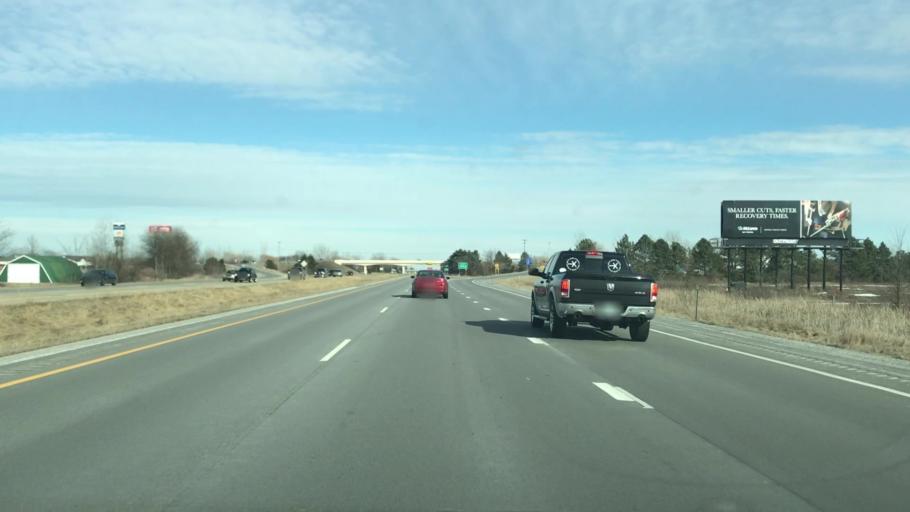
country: US
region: Michigan
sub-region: Bay County
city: Auburn
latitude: 43.5969
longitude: -84.0946
